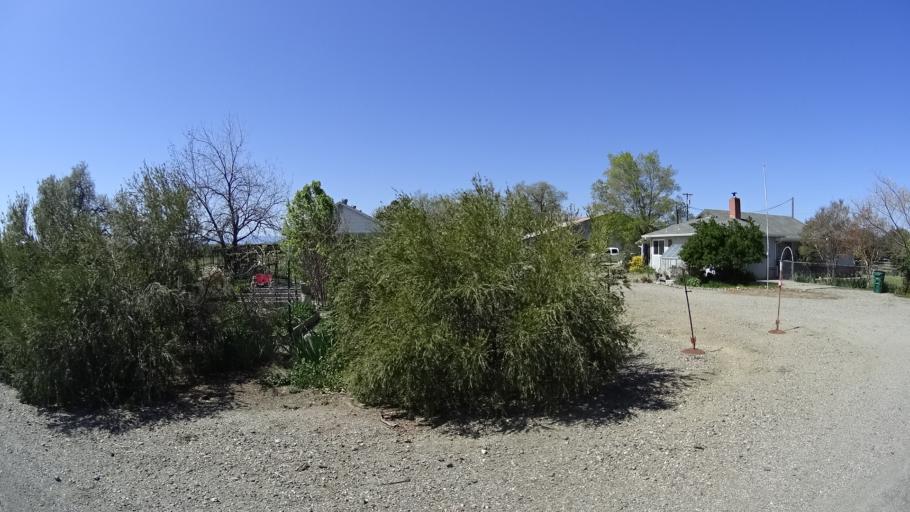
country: US
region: California
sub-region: Glenn County
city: Orland
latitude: 39.7690
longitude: -122.2387
